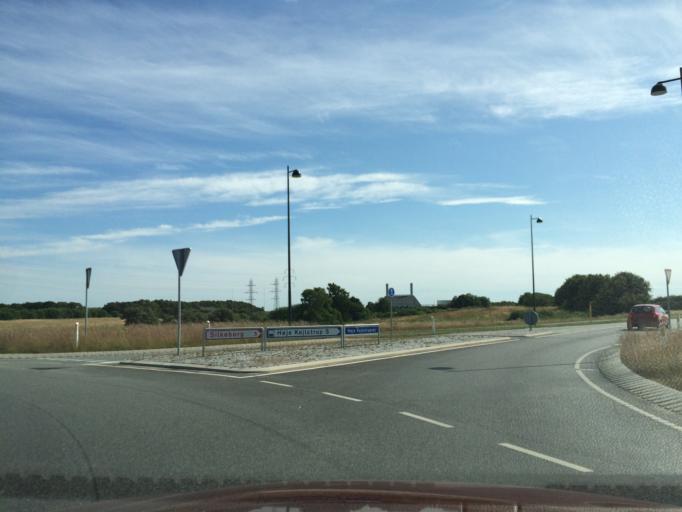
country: DK
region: Central Jutland
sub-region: Silkeborg Kommune
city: Silkeborg
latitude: 56.2080
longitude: 9.5621
